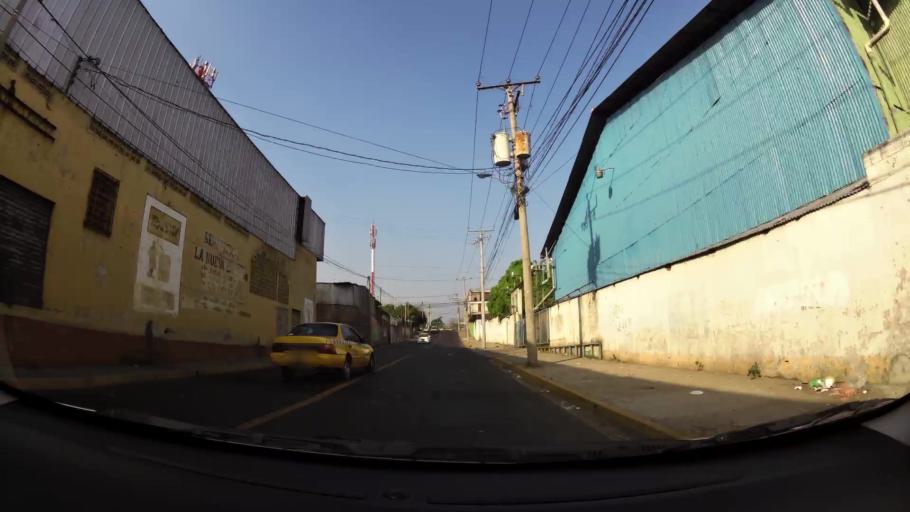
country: SV
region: San Salvador
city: San Salvador
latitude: 13.6983
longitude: -89.1767
